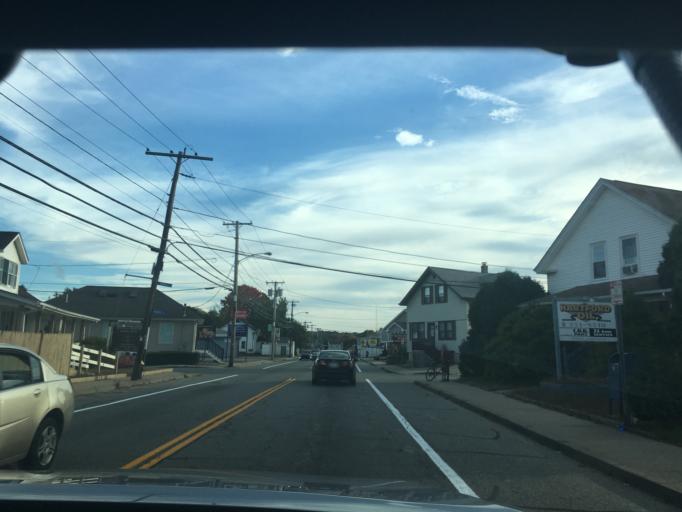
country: US
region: Rhode Island
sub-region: Providence County
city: North Providence
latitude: 41.8298
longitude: -71.4730
